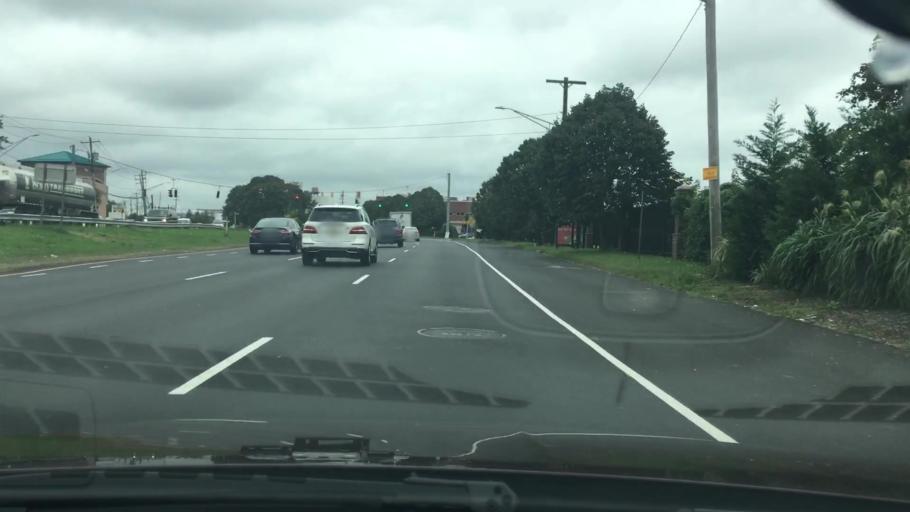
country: US
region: New York
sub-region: Nassau County
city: Bethpage
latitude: 40.7410
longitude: -73.4958
